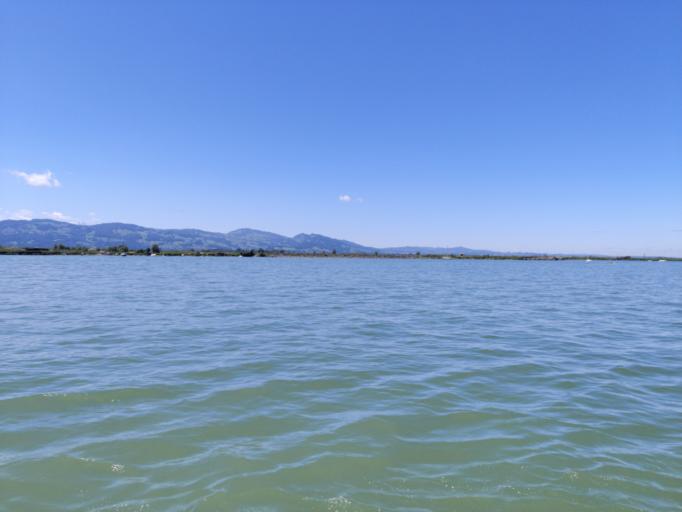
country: DE
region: Bavaria
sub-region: Swabia
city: Lindau
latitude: 47.5171
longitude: 9.6646
